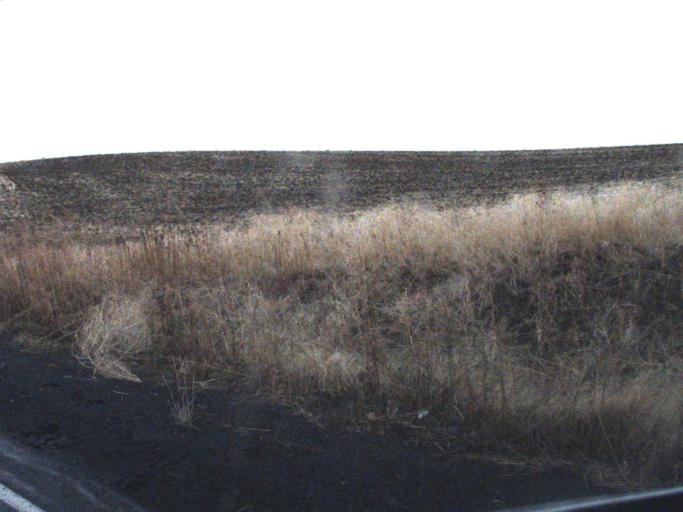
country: US
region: Washington
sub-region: Lincoln County
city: Davenport
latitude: 47.7242
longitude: -118.1535
